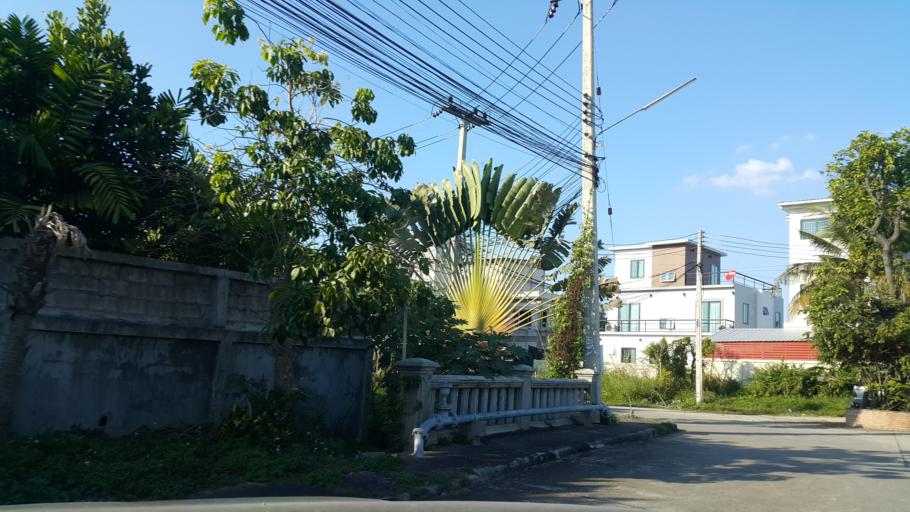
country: TH
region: Chiang Mai
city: Chiang Mai
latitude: 18.7667
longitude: 98.9592
